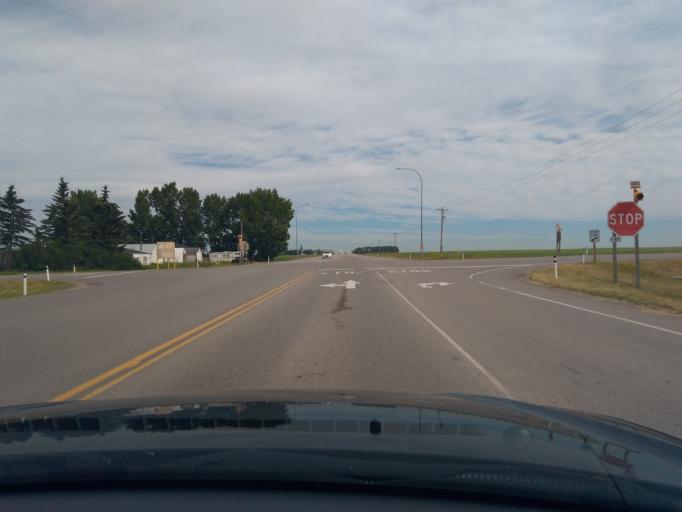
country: CA
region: Alberta
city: Didsbury
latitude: 51.6635
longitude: -114.0959
